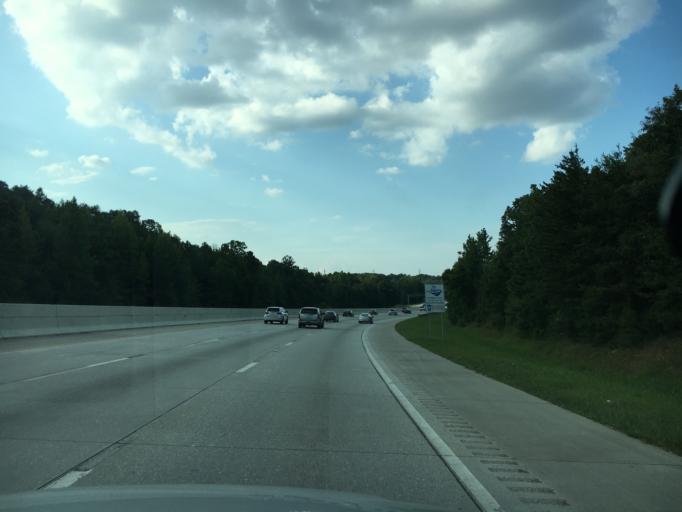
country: US
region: South Carolina
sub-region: Greenville County
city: Mauldin
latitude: 34.7841
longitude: -82.2807
